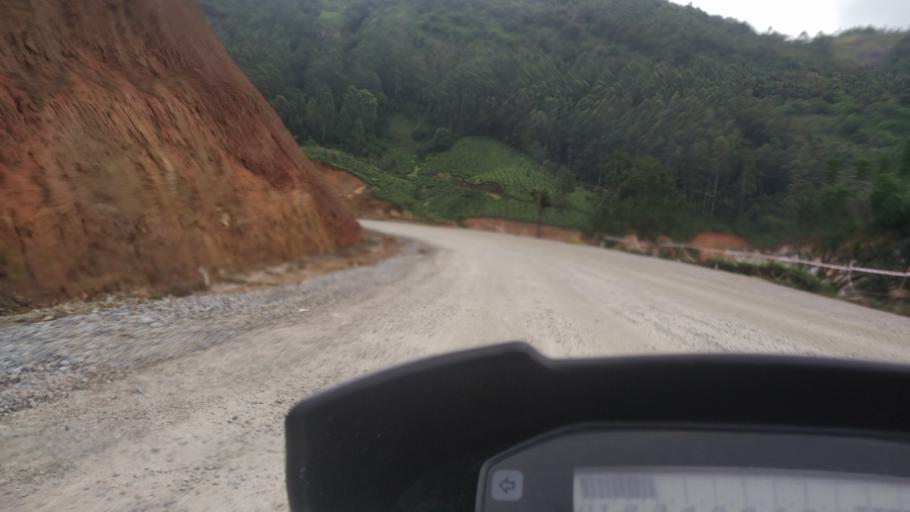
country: IN
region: Kerala
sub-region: Idukki
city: Munnar
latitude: 10.0351
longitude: 77.1526
